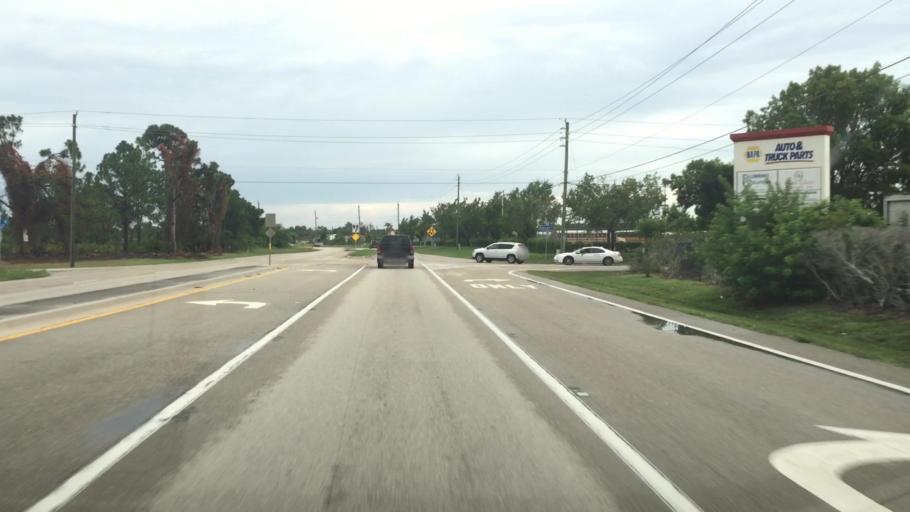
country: US
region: Florida
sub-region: Lee County
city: Gateway
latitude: 26.6161
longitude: -81.7488
